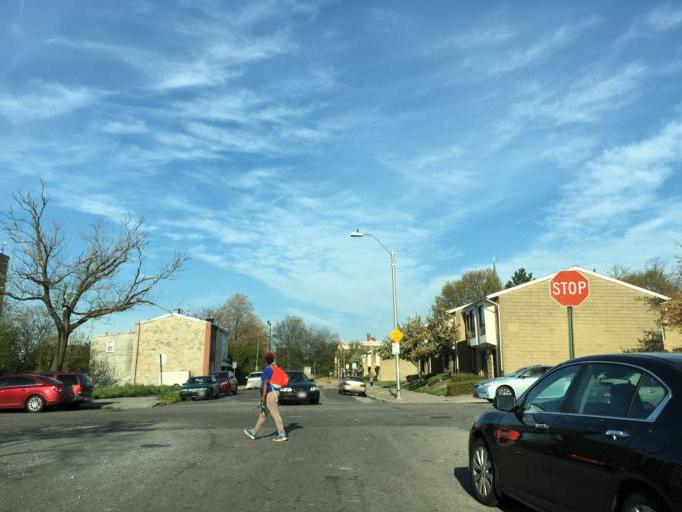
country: US
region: Maryland
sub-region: City of Baltimore
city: Baltimore
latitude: 39.3004
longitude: -76.5974
